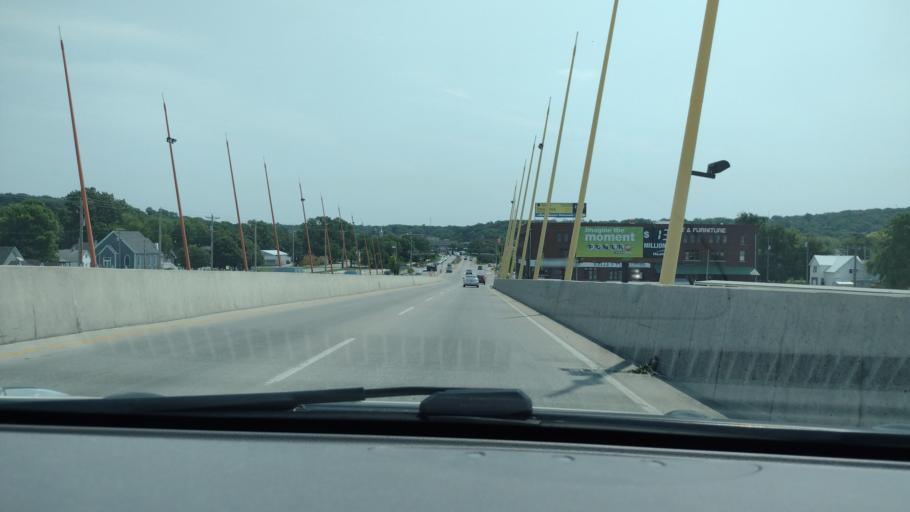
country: US
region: Iowa
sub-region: Pottawattamie County
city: Council Bluffs
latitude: 41.2618
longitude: -95.8593
